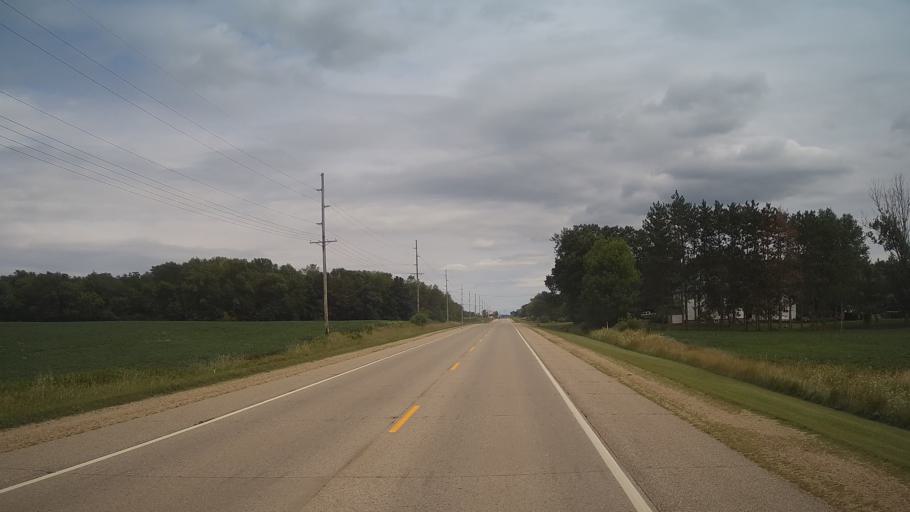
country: US
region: Wisconsin
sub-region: Green Lake County
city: Berlin
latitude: 44.0410
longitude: -89.0013
